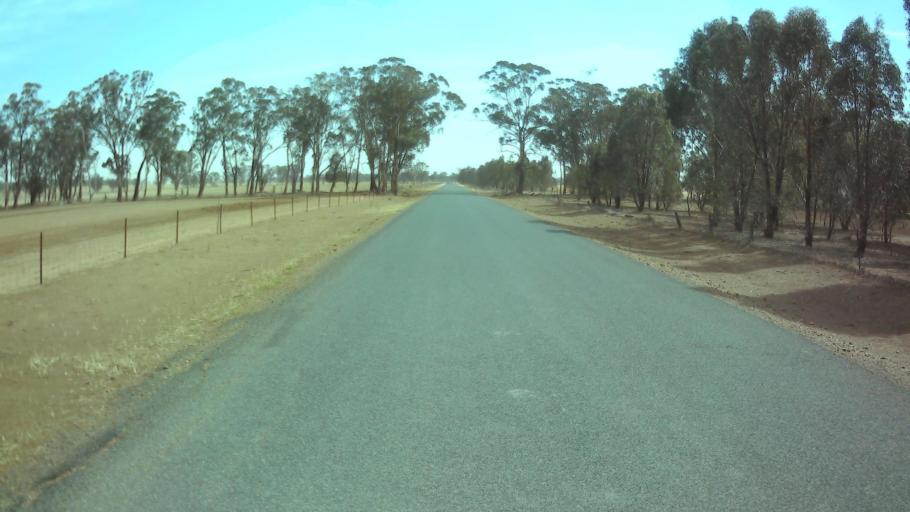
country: AU
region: New South Wales
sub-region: Weddin
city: Grenfell
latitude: -33.7163
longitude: 148.0007
